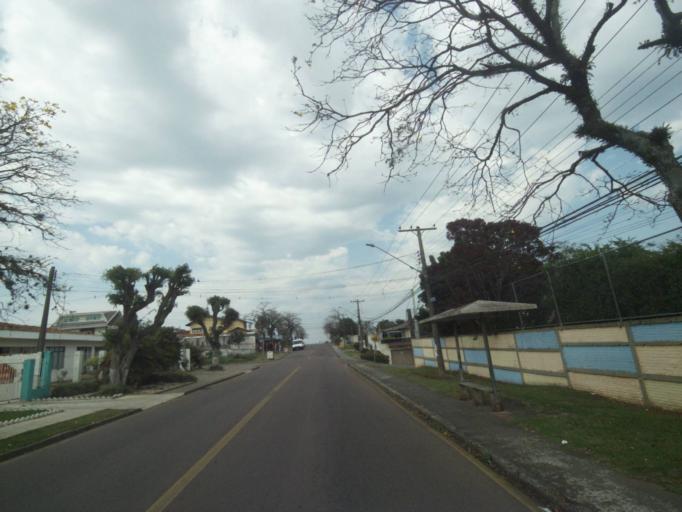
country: BR
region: Parana
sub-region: Sao Jose Dos Pinhais
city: Sao Jose dos Pinhais
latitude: -25.5248
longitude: -49.2566
